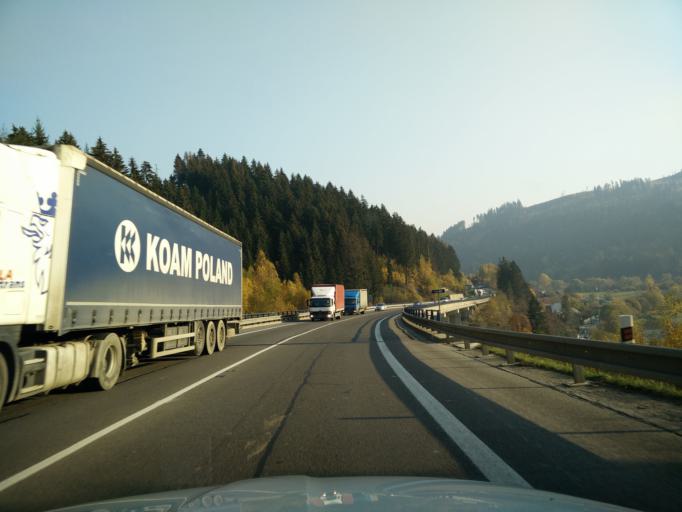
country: SK
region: Zilinsky
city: Cadca
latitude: 49.4311
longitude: 18.8122
